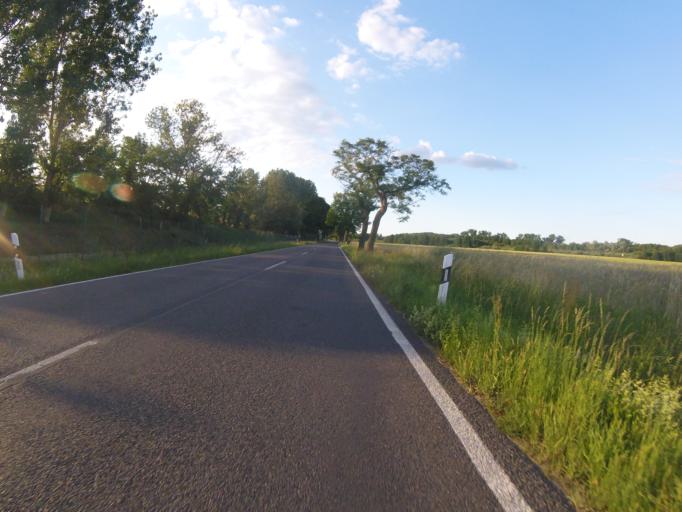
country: DE
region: Brandenburg
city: Mittenwalde
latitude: 52.2295
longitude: 13.5488
